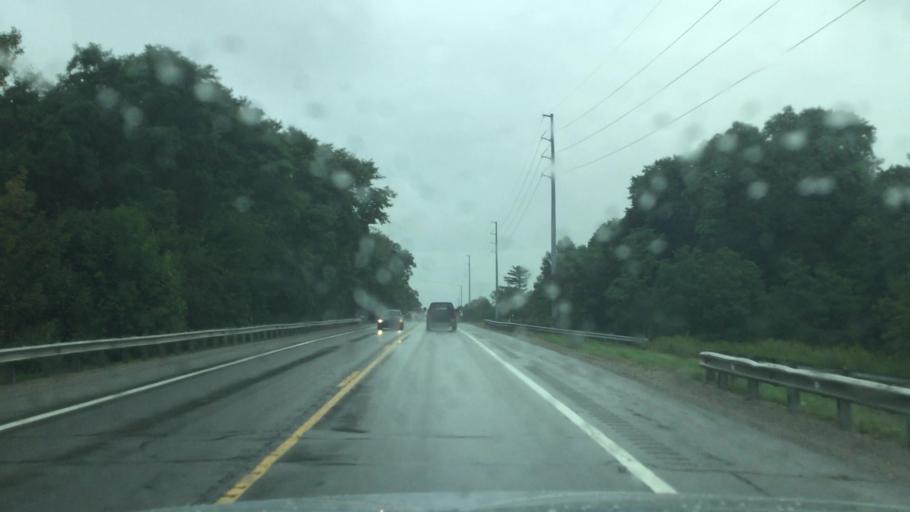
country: US
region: Michigan
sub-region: Livingston County
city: Howell
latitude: 42.6298
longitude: -83.8698
